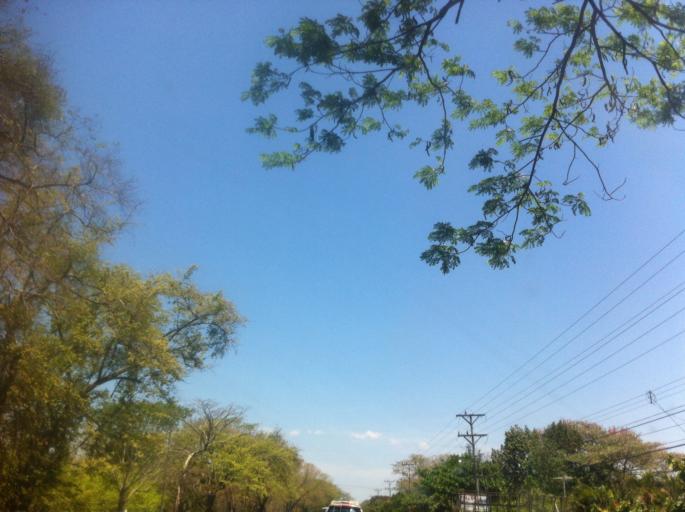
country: CR
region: Guanacaste
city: Sardinal
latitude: 10.5057
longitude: -85.5745
